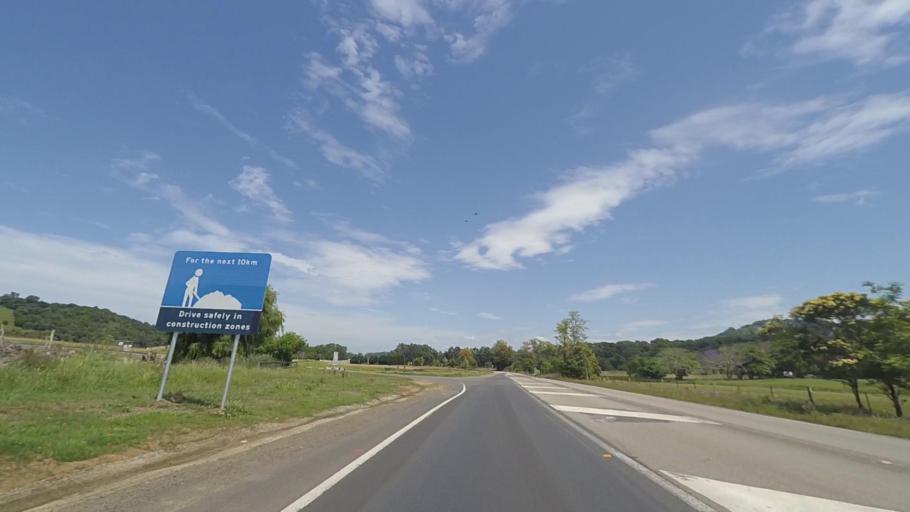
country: AU
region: New South Wales
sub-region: Kiama
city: Gerringong
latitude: -34.7418
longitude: 150.7620
